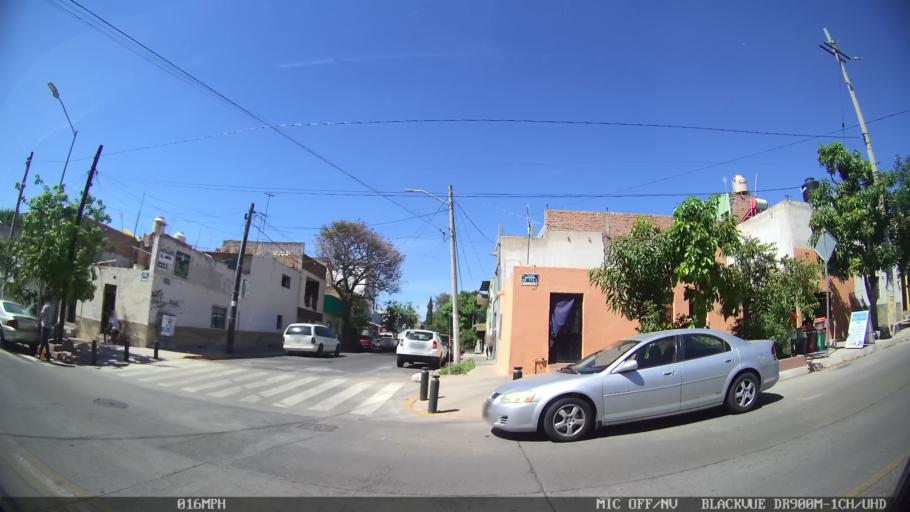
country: MX
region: Jalisco
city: Tlaquepaque
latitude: 20.6906
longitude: -103.2848
